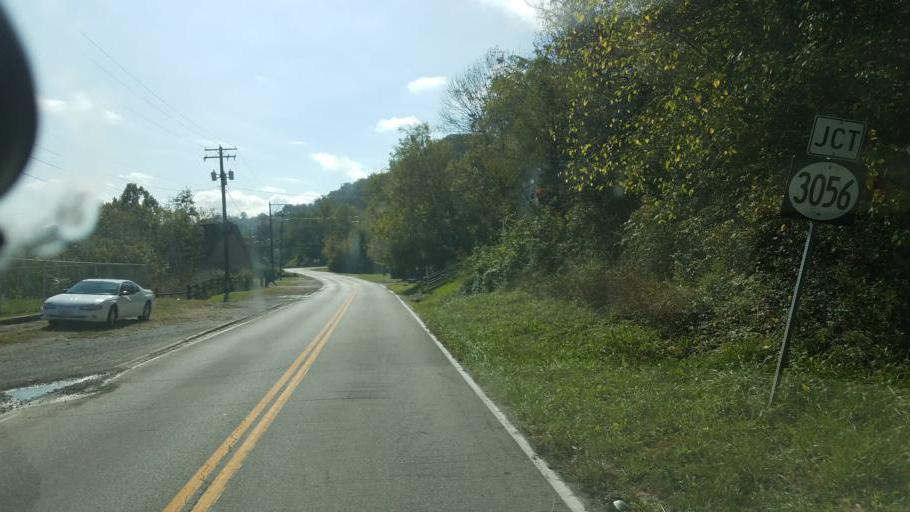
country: US
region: Ohio
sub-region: Brown County
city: Aberdeen
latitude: 38.6597
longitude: -83.7781
